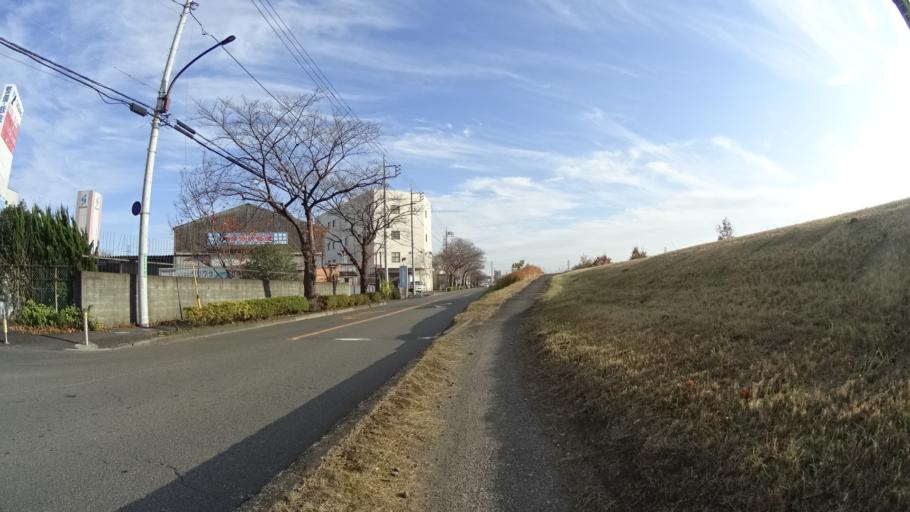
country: JP
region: Tokyo
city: Hino
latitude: 35.6694
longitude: 139.4326
